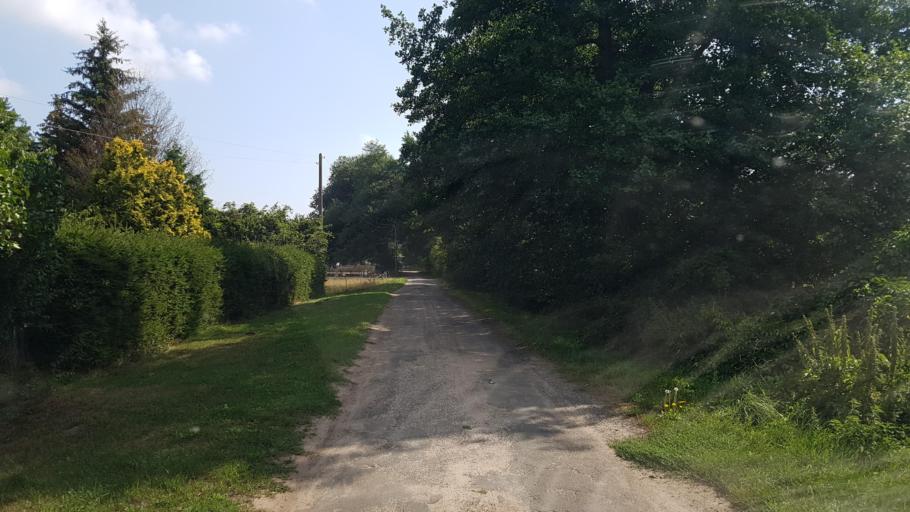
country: DE
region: Brandenburg
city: Bruck
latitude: 52.1938
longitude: 12.7986
